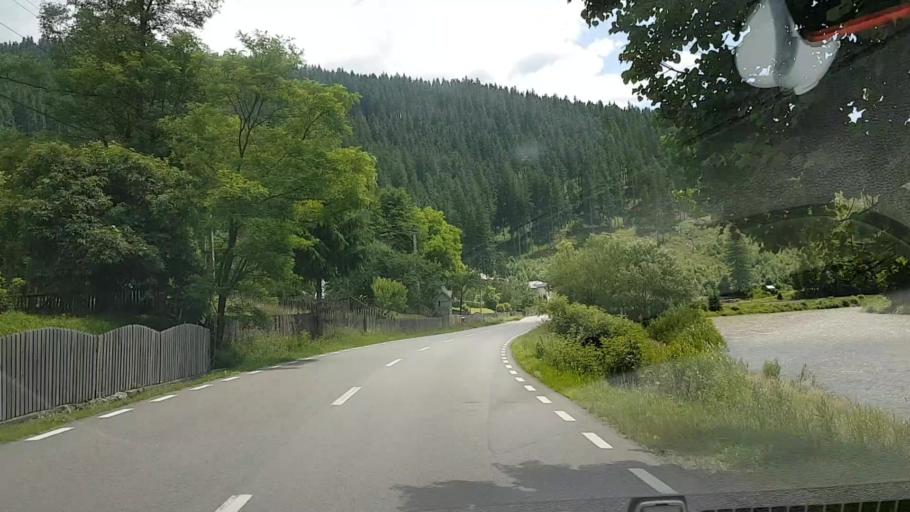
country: RO
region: Suceava
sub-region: Comuna Crucea
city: Crucea
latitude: 47.3566
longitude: 25.6130
